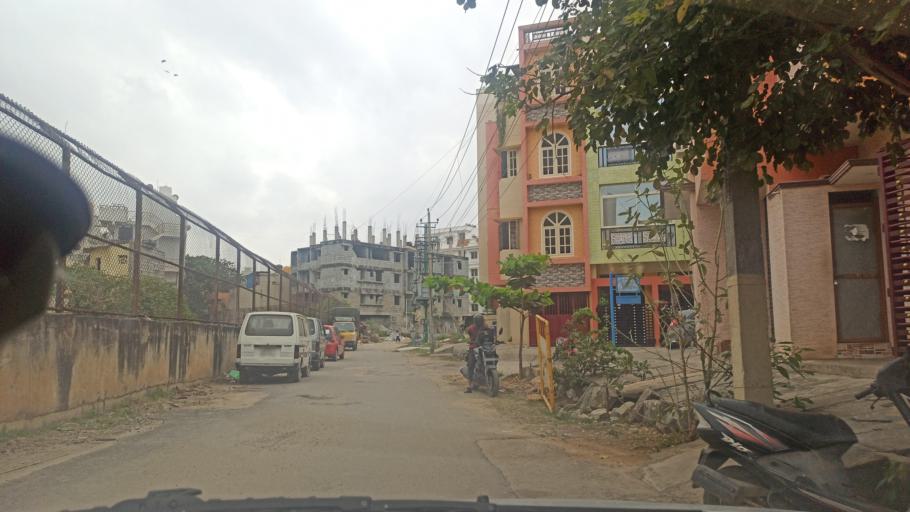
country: IN
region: Karnataka
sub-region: Bangalore Urban
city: Yelahanka
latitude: 13.0376
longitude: 77.6012
